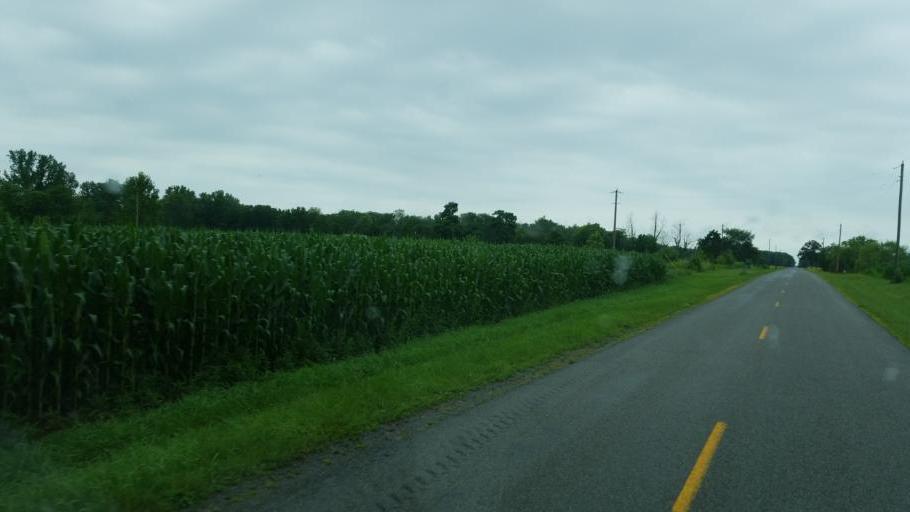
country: US
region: Ohio
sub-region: Hardin County
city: Kenton
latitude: 40.5099
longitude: -83.4818
